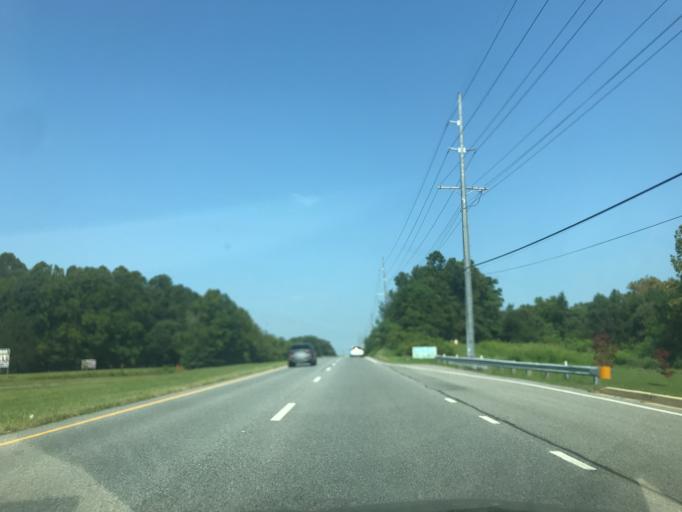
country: US
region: Maryland
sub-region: Calvert County
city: Owings
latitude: 38.6759
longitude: -76.6251
